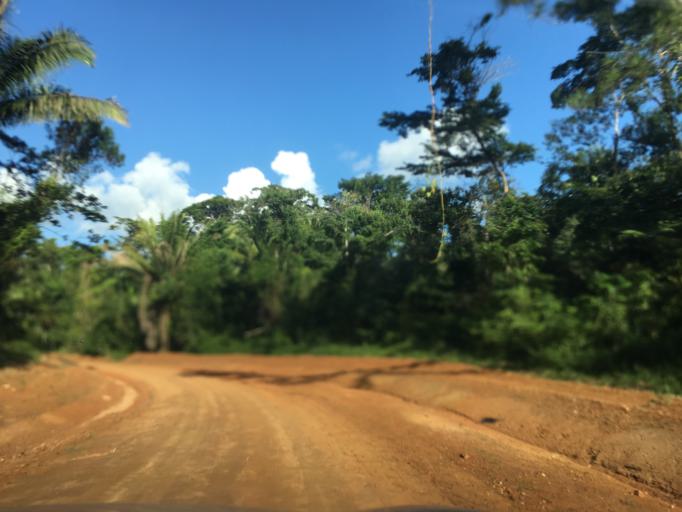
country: BZ
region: Stann Creek
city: Placencia
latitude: 16.7850
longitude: -88.4497
